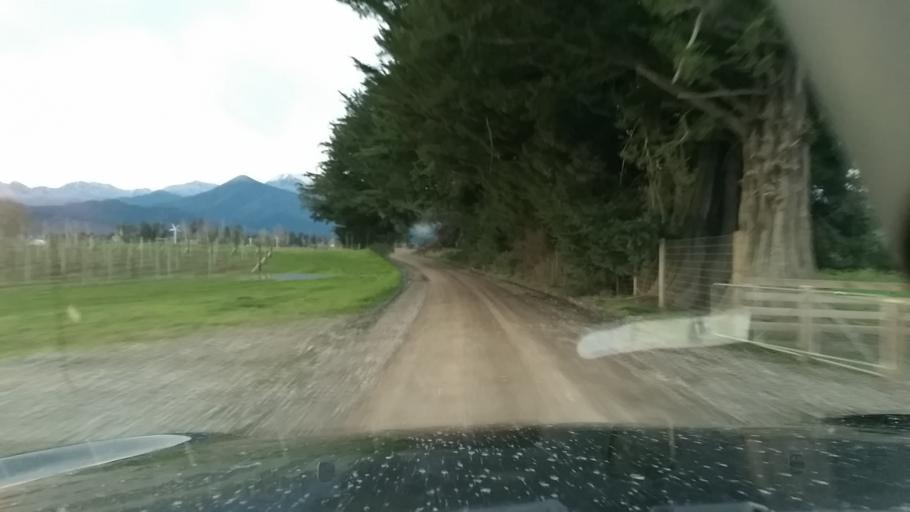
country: NZ
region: Nelson
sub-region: Nelson City
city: Nelson
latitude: -41.5831
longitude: 173.5098
